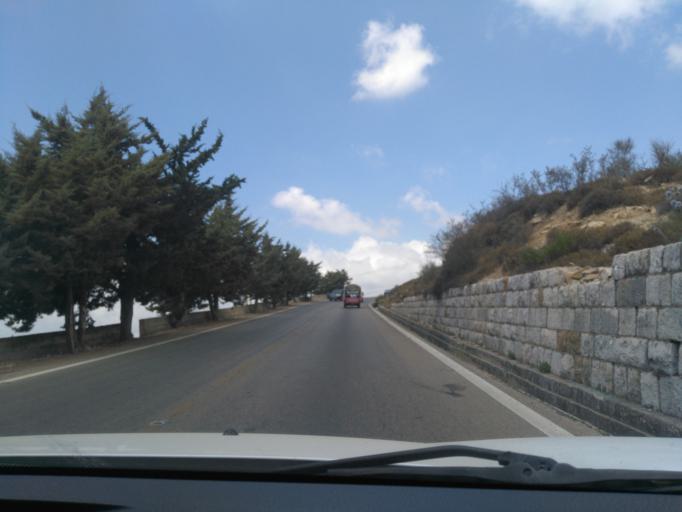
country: LB
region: Mont-Liban
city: Beit ed Dine
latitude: 33.6956
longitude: 35.6142
